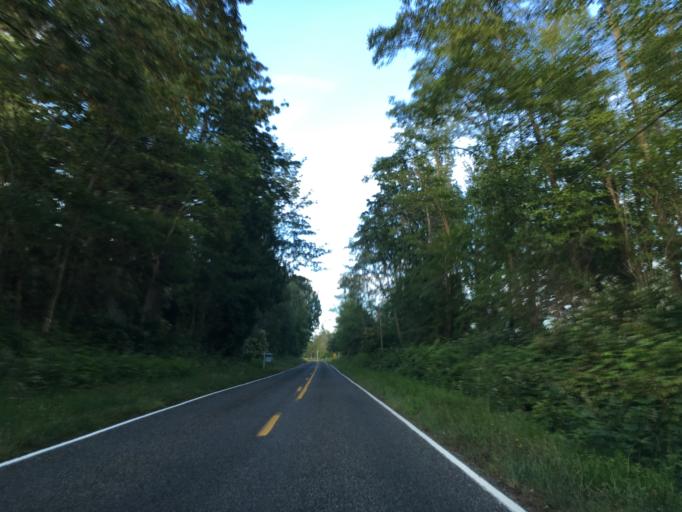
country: CA
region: British Columbia
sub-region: Greater Vancouver Regional District
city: White Rock
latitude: 48.9573
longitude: -122.8120
